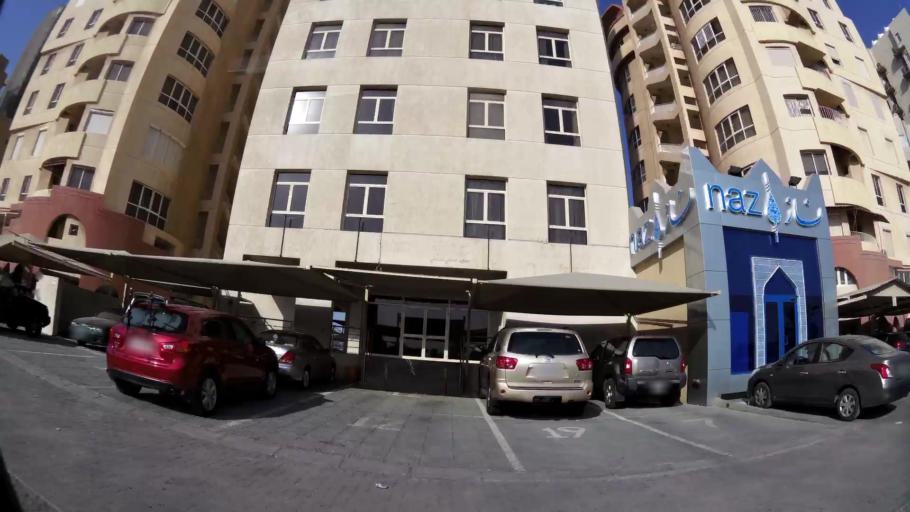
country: KW
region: Muhafazat Hawalli
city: As Salimiyah
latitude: 29.3330
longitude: 48.0761
